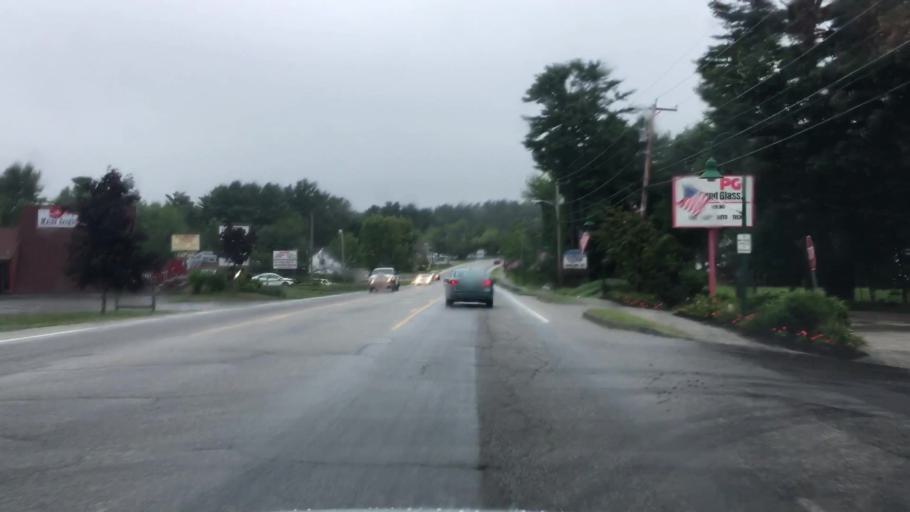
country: US
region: Maine
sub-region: Cumberland County
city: Raymond
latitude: 43.8852
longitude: -70.4649
